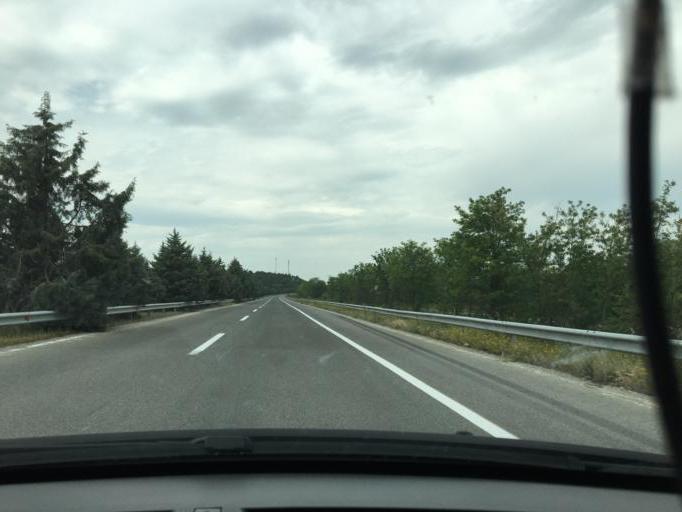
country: MK
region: Negotino
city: Negotino
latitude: 41.5277
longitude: 22.0617
